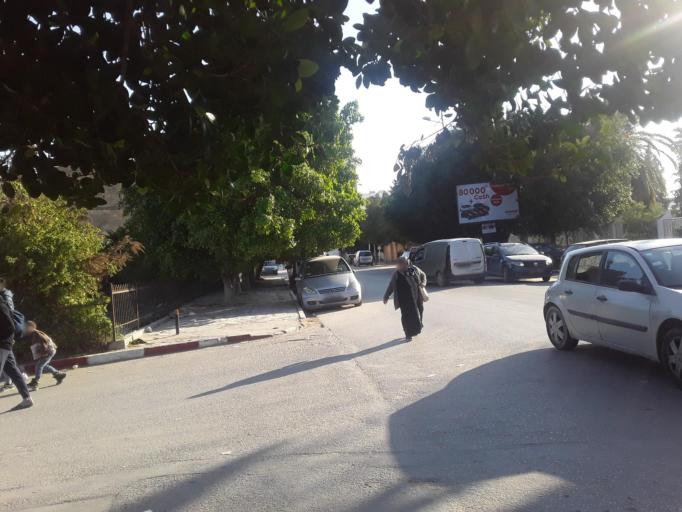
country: TN
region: Al Qayrawan
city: Kairouan
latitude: 35.6804
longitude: 10.0985
